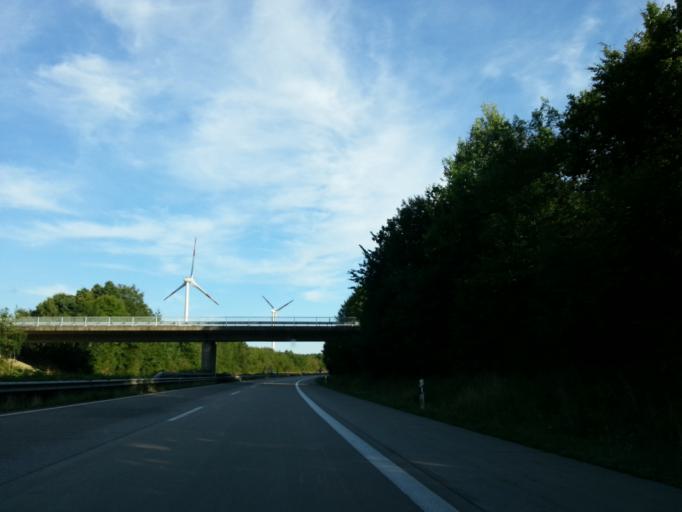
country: DE
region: Rheinland-Pfalz
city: Bescheid
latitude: 49.7550
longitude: 6.8692
